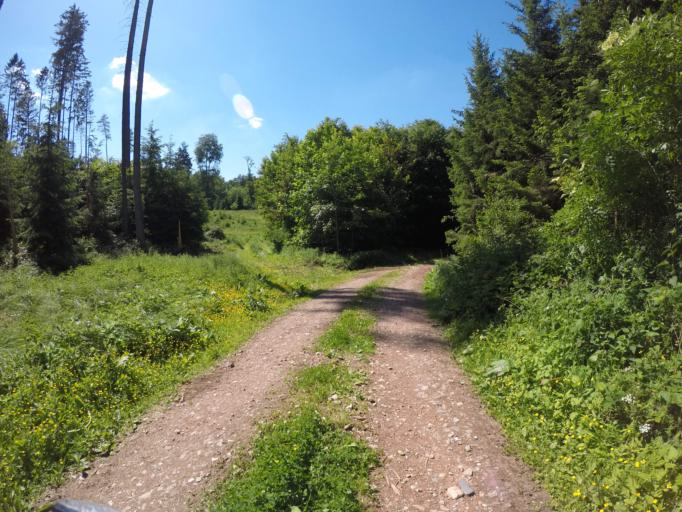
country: DE
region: Bavaria
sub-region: Lower Bavaria
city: Kumhausen
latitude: 48.5102
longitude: 12.1862
